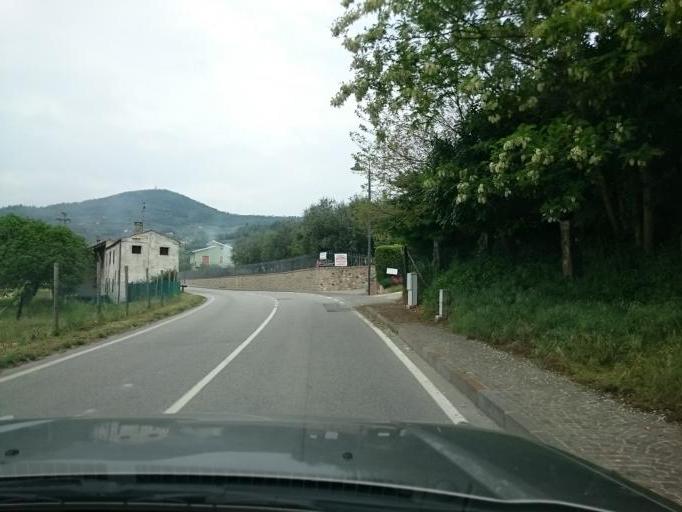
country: IT
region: Veneto
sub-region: Provincia di Padova
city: Arqua Petrarca
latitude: 45.2618
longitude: 11.7128
